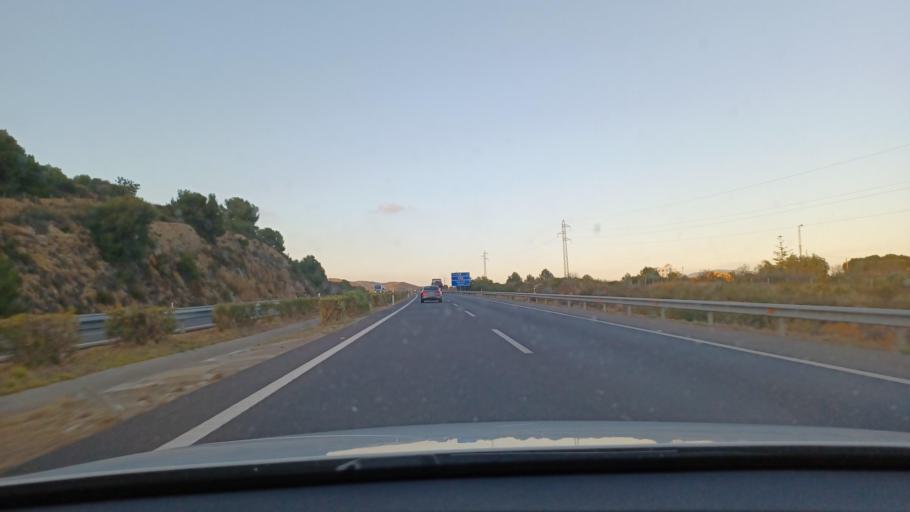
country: ES
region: Valencia
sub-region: Provincia de Castello
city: Torreblanca
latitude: 40.1904
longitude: 0.1718
